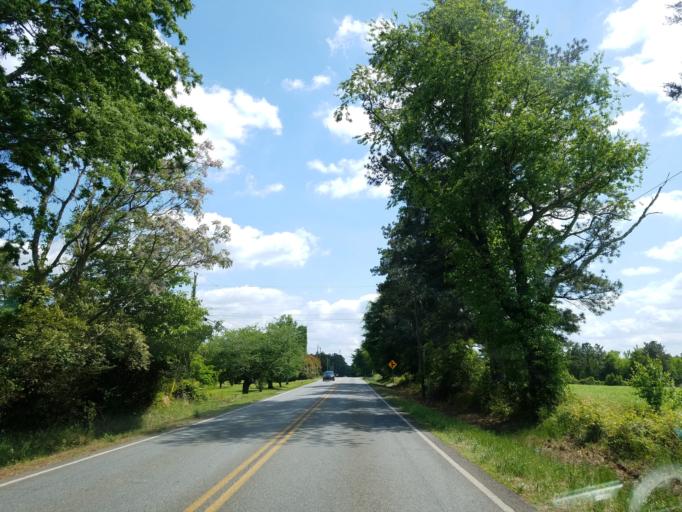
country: US
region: Georgia
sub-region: Monroe County
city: Forsyth
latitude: 33.0721
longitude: -83.9561
